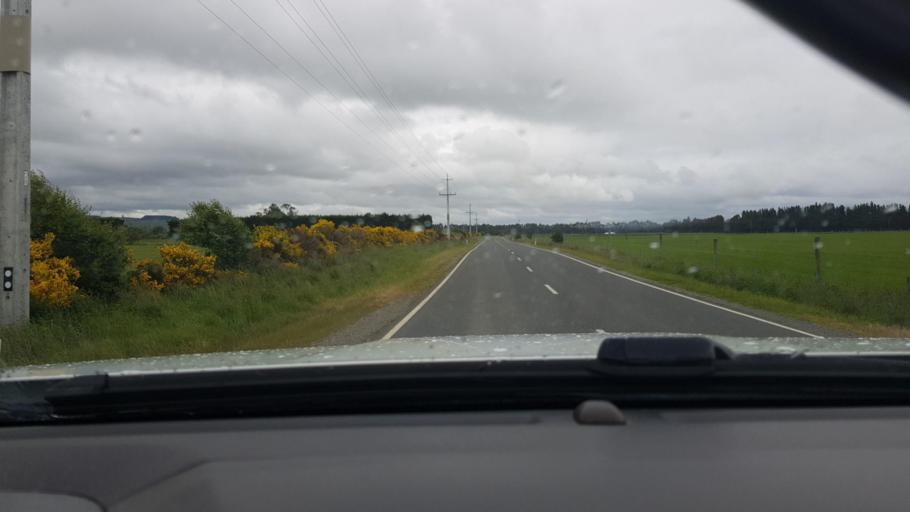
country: NZ
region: Southland
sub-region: Southland District
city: Winton
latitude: -45.8608
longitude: 168.3591
